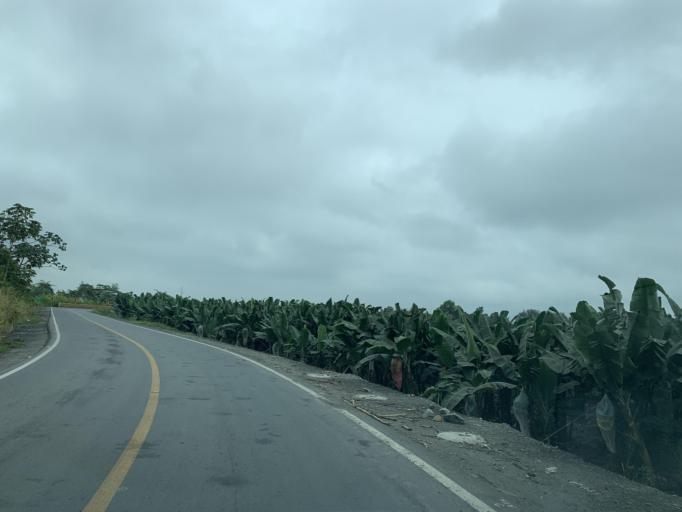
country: EC
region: Guayas
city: Coronel Marcelino Mariduena
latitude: -2.3007
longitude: -79.5028
